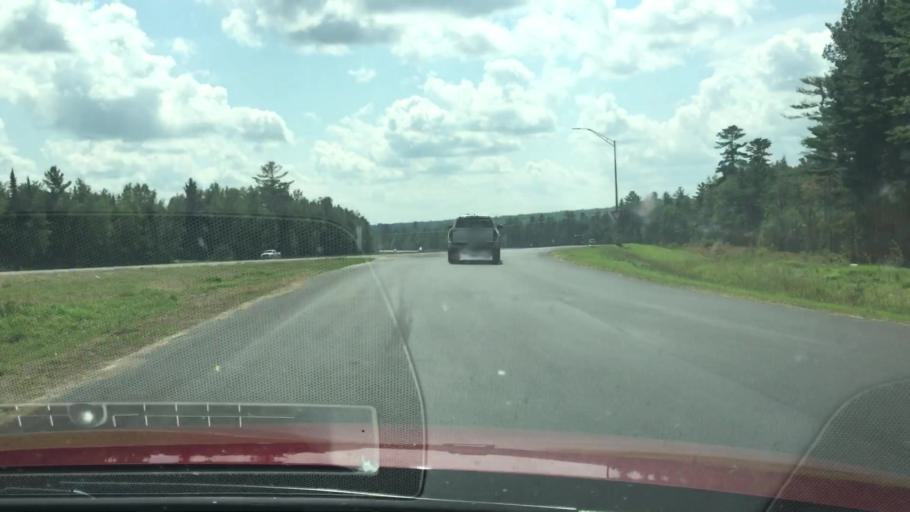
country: US
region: Maine
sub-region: Penobscot County
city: Medway
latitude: 45.5949
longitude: -68.5393
